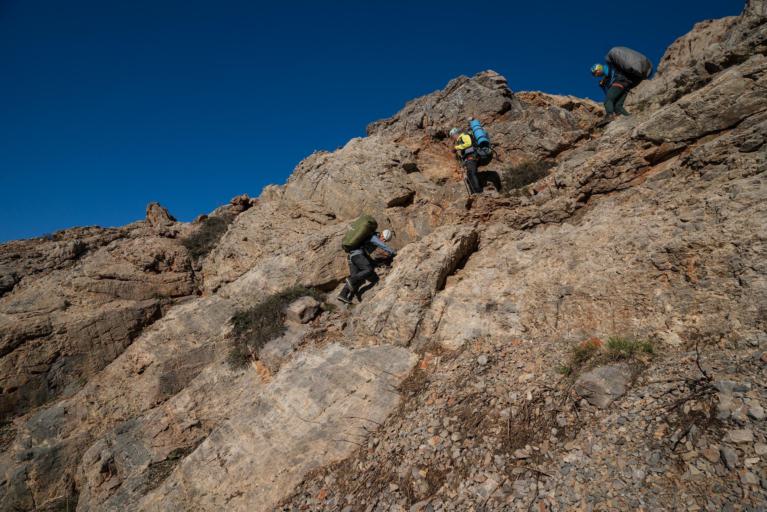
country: KZ
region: Ongtustik Qazaqstan
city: Ashchysay
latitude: 43.7638
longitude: 68.7791
